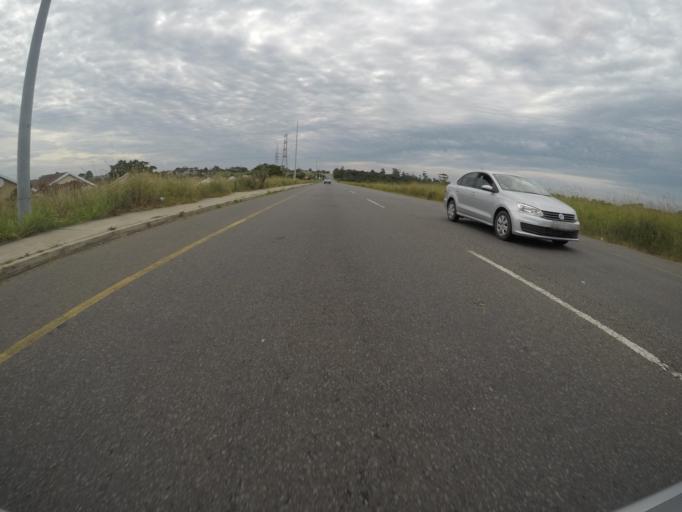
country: ZA
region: Eastern Cape
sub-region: Buffalo City Metropolitan Municipality
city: East London
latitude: -32.9775
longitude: 27.8575
